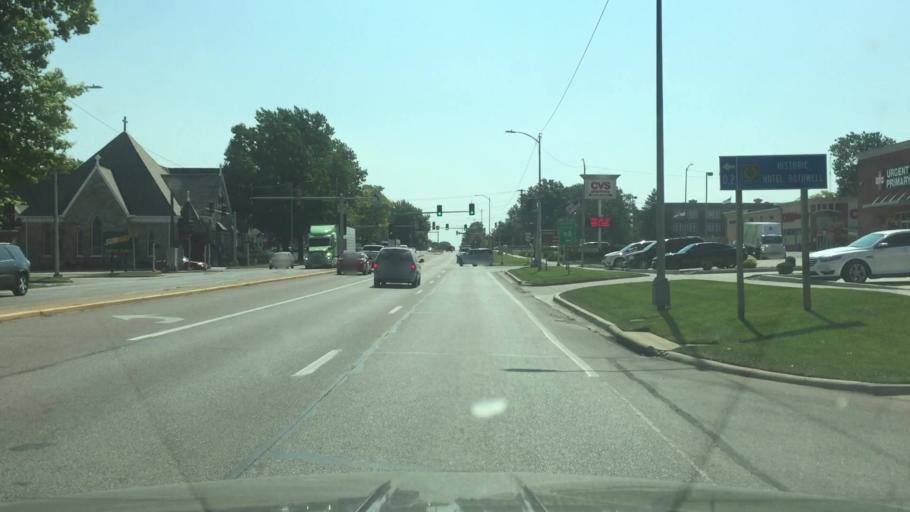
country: US
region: Missouri
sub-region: Pettis County
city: Sedalia
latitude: 38.7042
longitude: -93.2294
